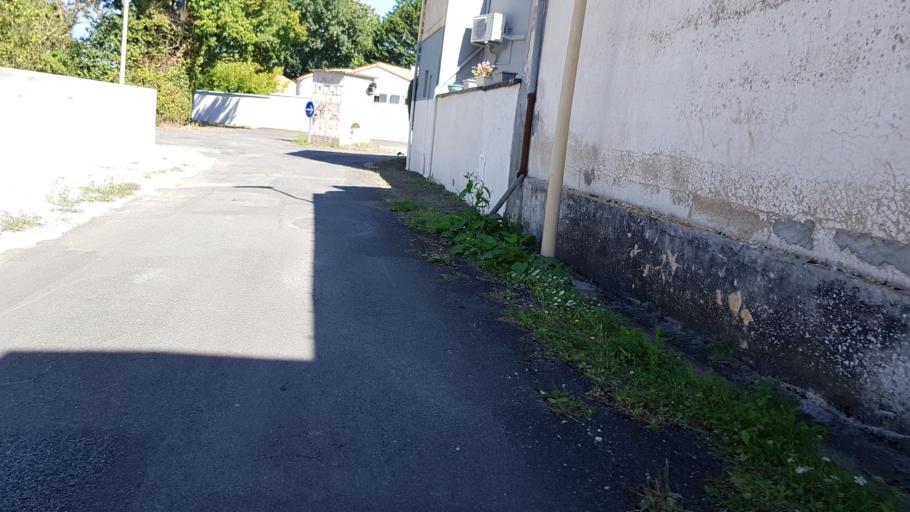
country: FR
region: Poitou-Charentes
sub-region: Departement des Deux-Sevres
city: Vouille
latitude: 46.3149
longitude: -0.3738
